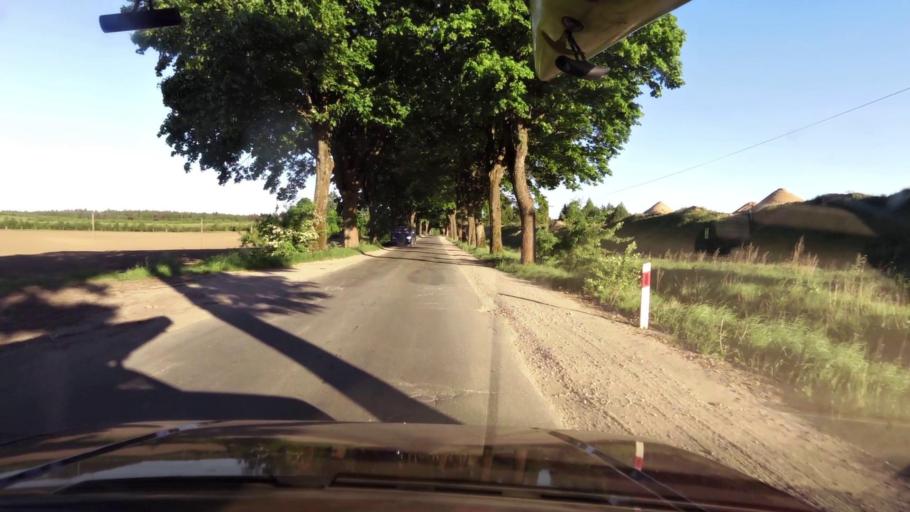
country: PL
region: West Pomeranian Voivodeship
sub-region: Powiat szczecinecki
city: Bialy Bor
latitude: 53.9366
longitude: 16.7934
